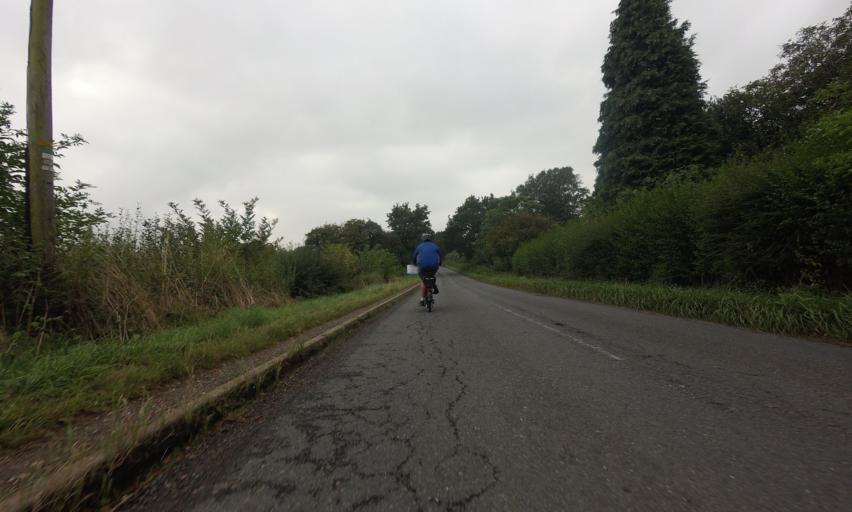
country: GB
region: England
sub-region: Gloucestershire
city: Winchcombe
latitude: 51.9689
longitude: -1.9731
